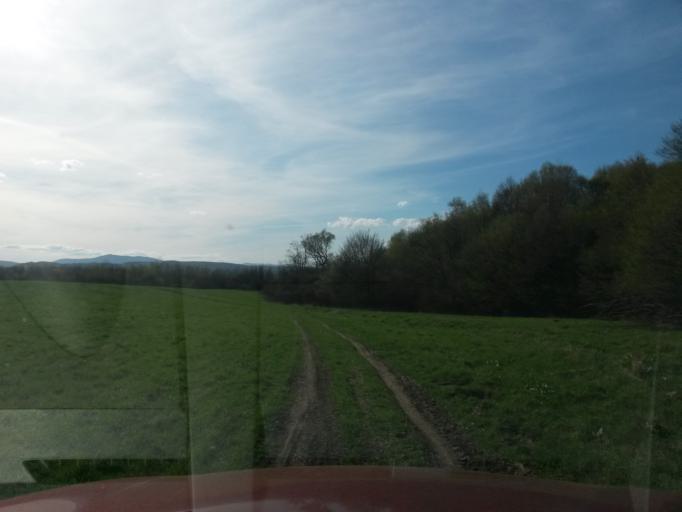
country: SK
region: Presovsky
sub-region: Okres Presov
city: Presov
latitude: 48.9266
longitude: 21.2181
